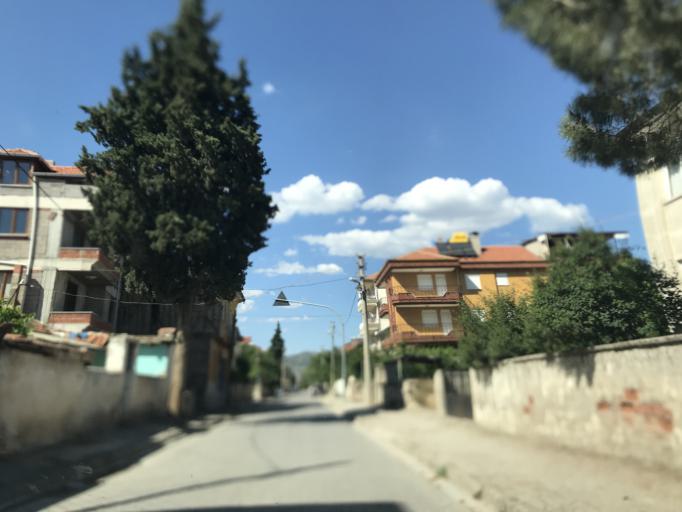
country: TR
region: Denizli
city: Civril
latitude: 38.3014
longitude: 29.7431
